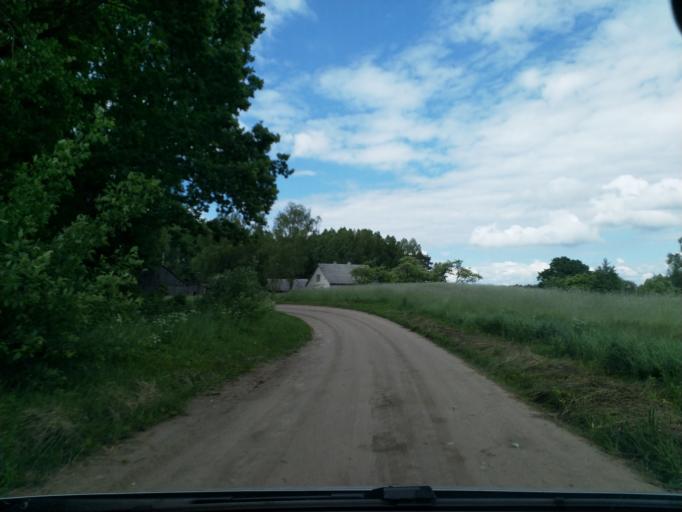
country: LV
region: Kuldigas Rajons
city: Kuldiga
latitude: 56.8365
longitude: 21.9563
